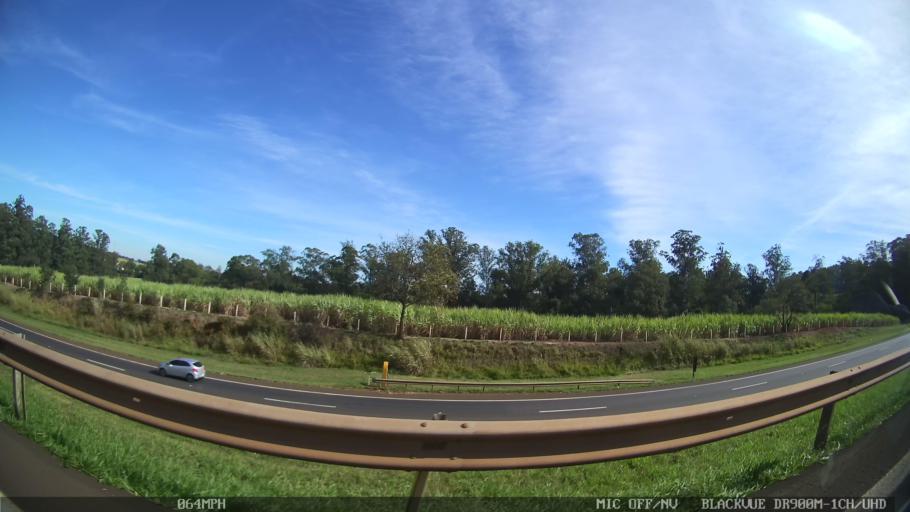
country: BR
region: Sao Paulo
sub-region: Araras
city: Araras
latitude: -22.3391
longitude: -47.3911
